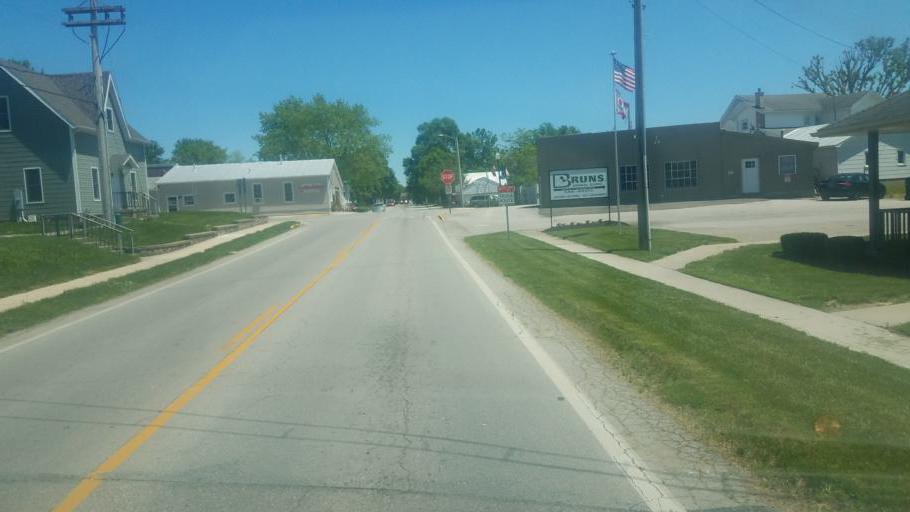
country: US
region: Ohio
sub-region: Darke County
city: Versailles
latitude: 40.2258
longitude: -84.4884
